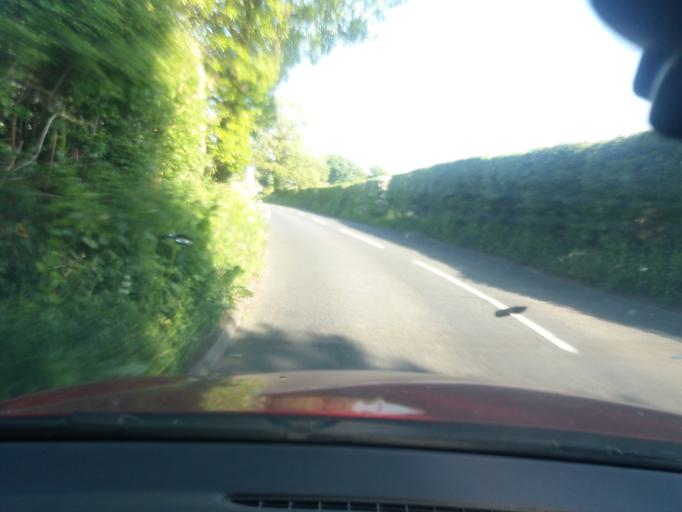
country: GB
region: England
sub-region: Borough of Wigan
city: Haigh
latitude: 53.6136
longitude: -2.5769
